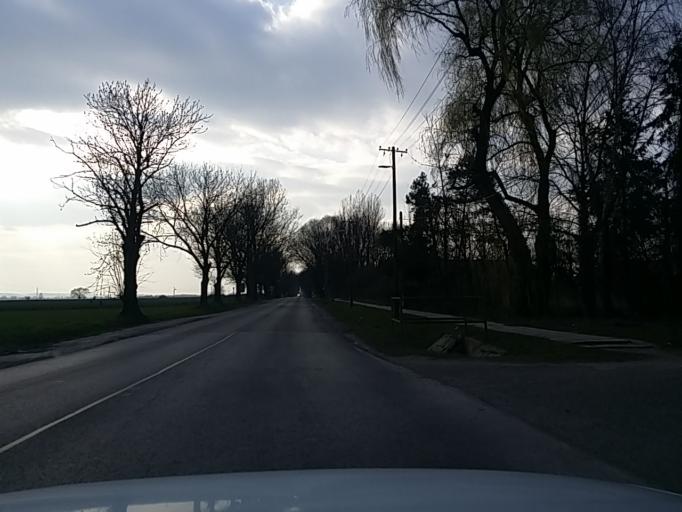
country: HU
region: Borsod-Abauj-Zemplen
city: Putnok
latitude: 48.2968
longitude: 20.4192
